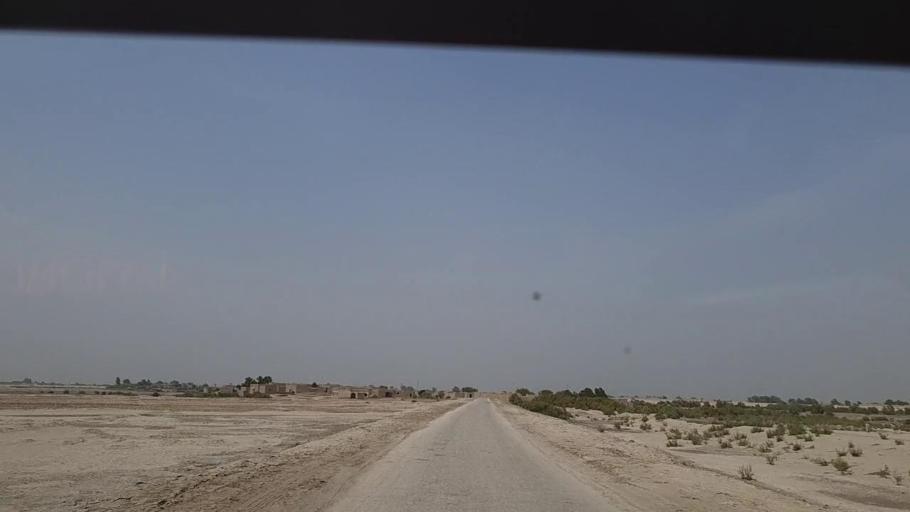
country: PK
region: Sindh
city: Khairpur Nathan Shah
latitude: 27.0649
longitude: 67.6487
